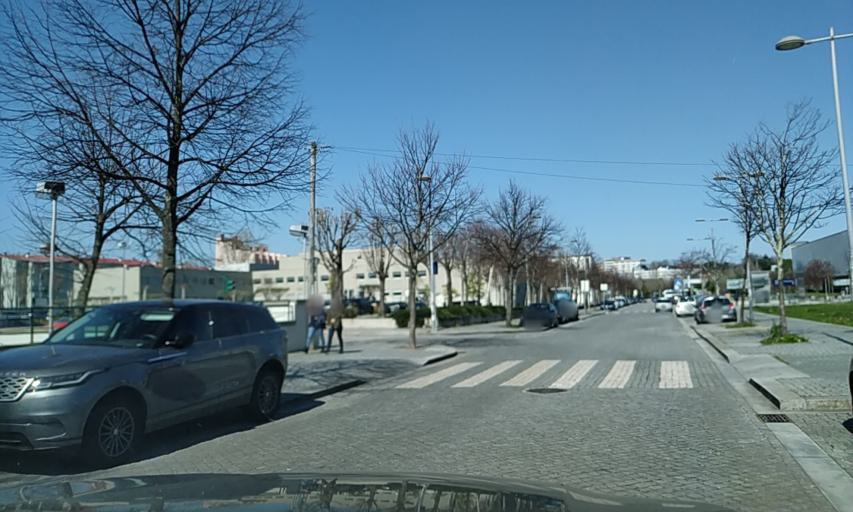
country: PT
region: Porto
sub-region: Porto
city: Porto
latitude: 41.1742
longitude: -8.6038
